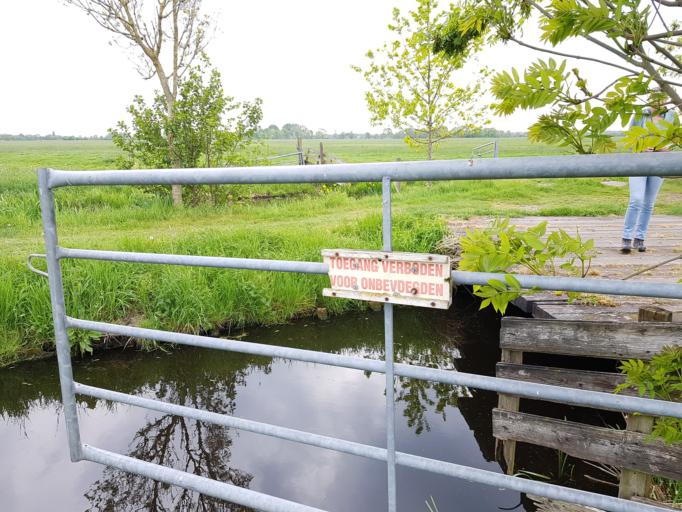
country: NL
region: South Holland
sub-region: Gemeente Vlist
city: Haastrecht
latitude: 51.9975
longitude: 4.7588
